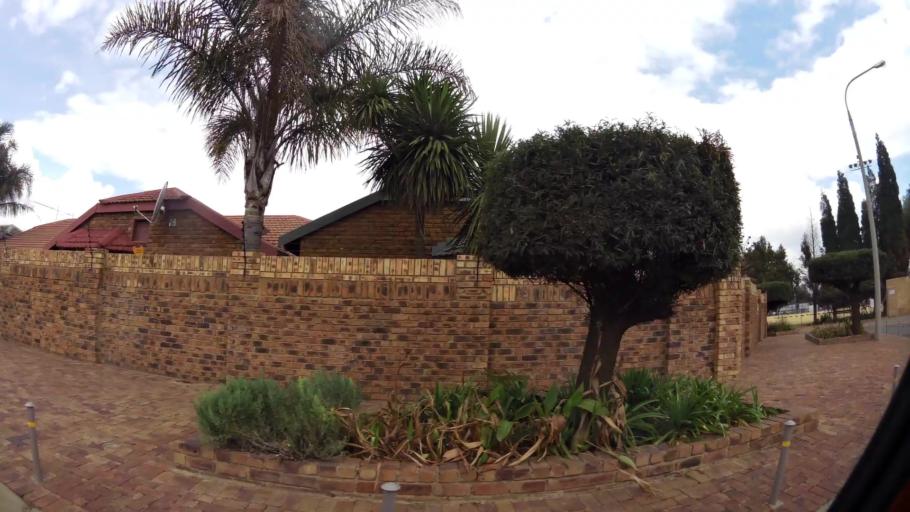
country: ZA
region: Gauteng
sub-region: Sedibeng District Municipality
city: Vanderbijlpark
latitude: -26.7367
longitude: 27.8494
